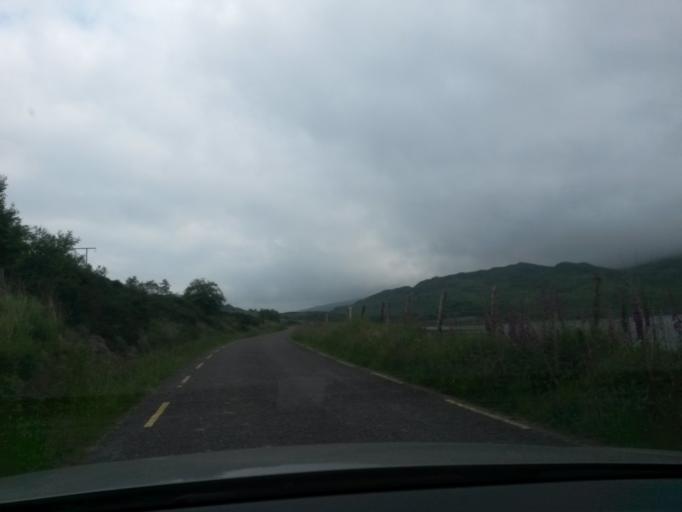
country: IE
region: Munster
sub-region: Ciarrai
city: Killorglin
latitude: 52.0080
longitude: -9.8162
